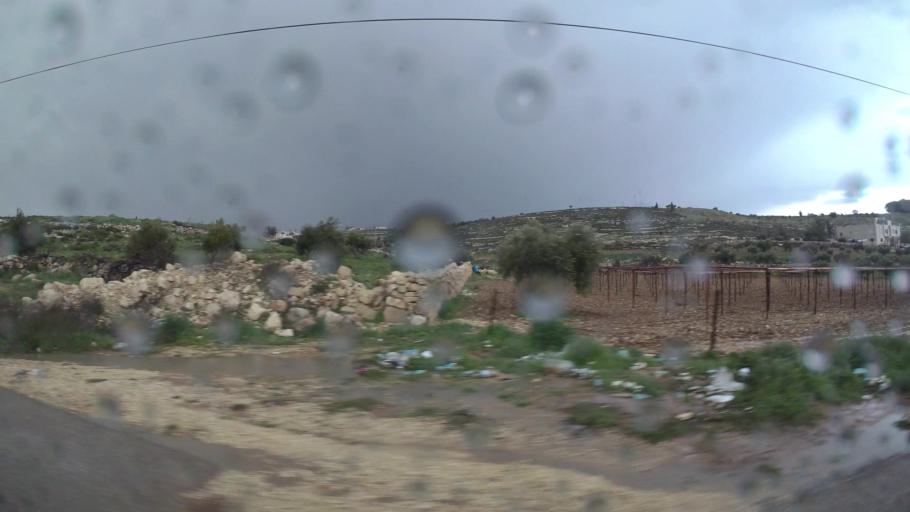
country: JO
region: Amman
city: Umm as Summaq
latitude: 31.8701
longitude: 35.8612
